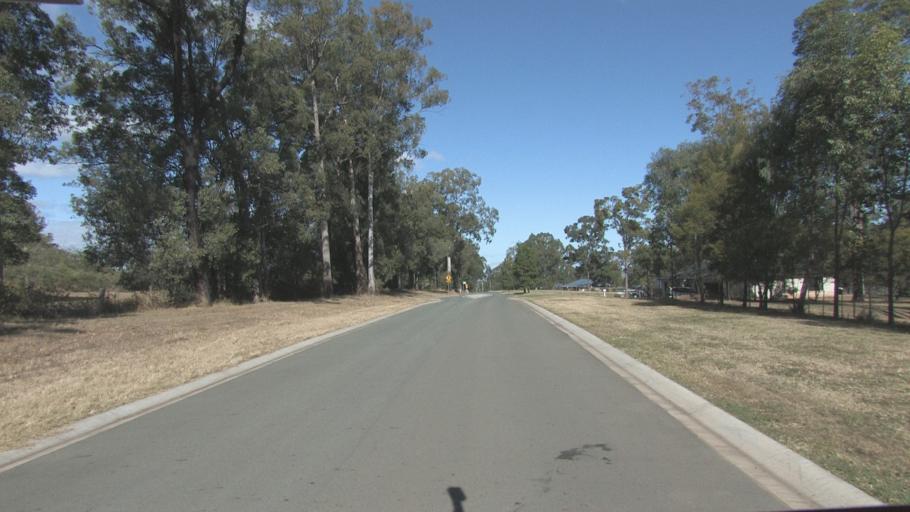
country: AU
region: Queensland
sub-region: Logan
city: Cedar Vale
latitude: -27.8927
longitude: 153.0022
